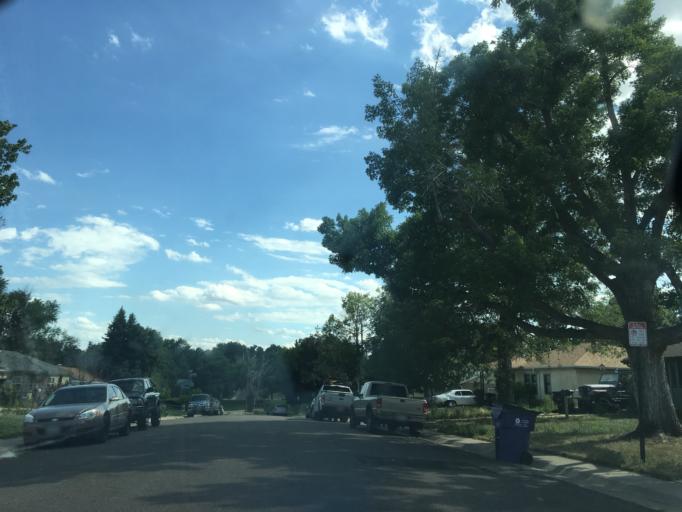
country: US
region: Colorado
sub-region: Arapahoe County
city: Sheridan
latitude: 39.6867
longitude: -105.0371
